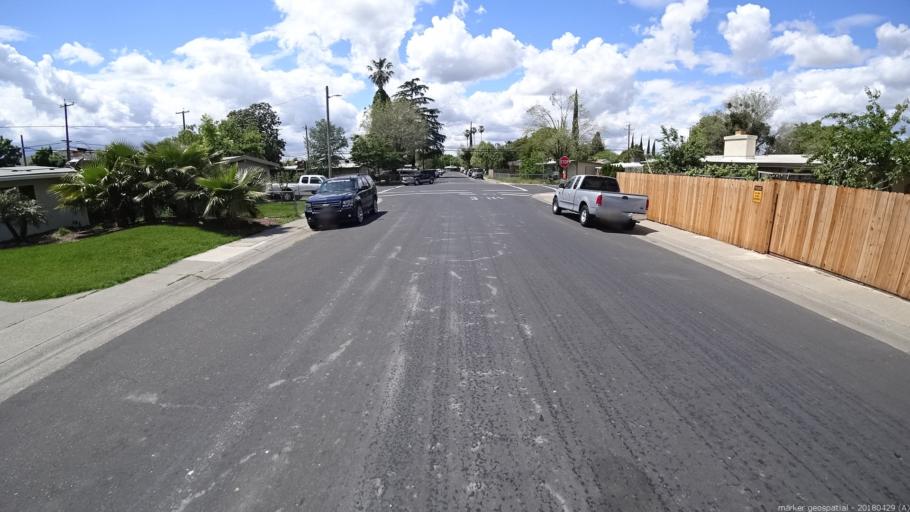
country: US
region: California
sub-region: Yolo County
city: West Sacramento
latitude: 38.5911
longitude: -121.5261
